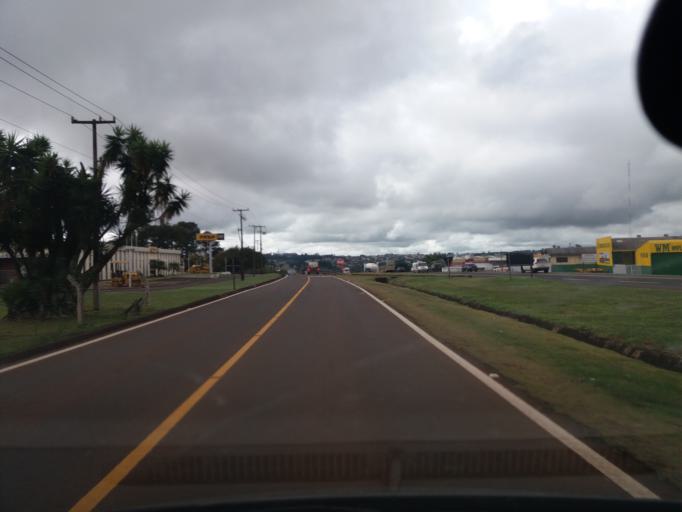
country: BR
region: Parana
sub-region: Cascavel
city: Cascavel
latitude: -24.9776
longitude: -53.4466
